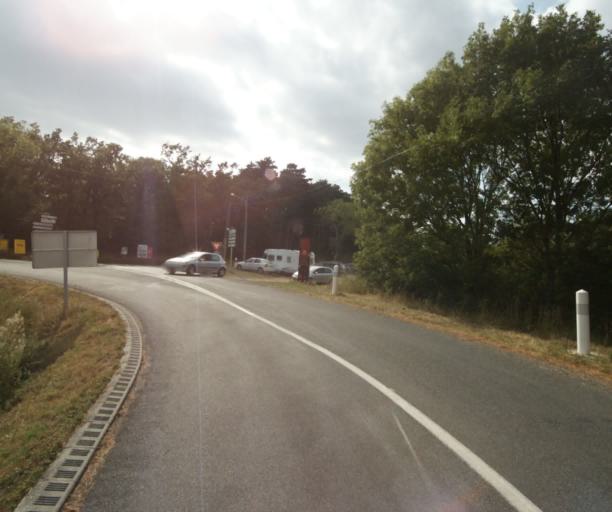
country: FR
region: Midi-Pyrenees
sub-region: Departement du Tarn
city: Soreze
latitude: 43.4394
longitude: 2.0353
